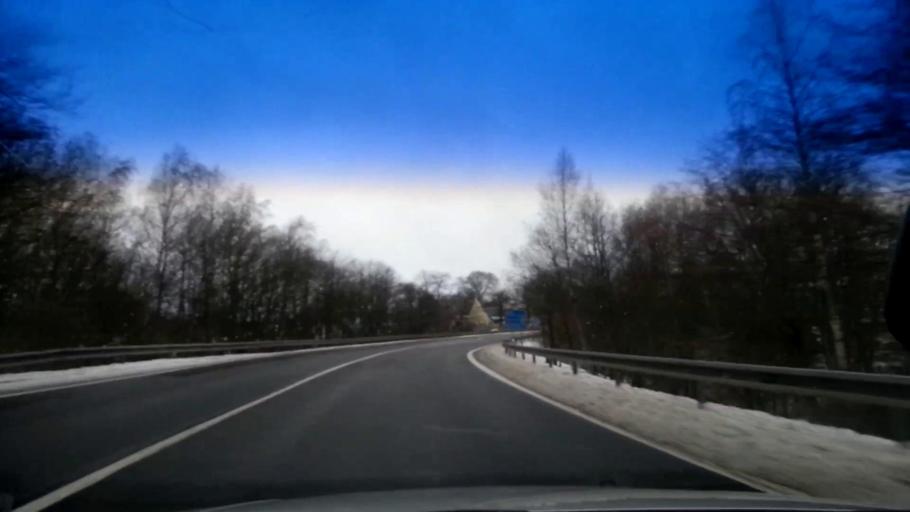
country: CZ
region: Karlovarsky
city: Hazlov
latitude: 50.1547
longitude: 12.2745
